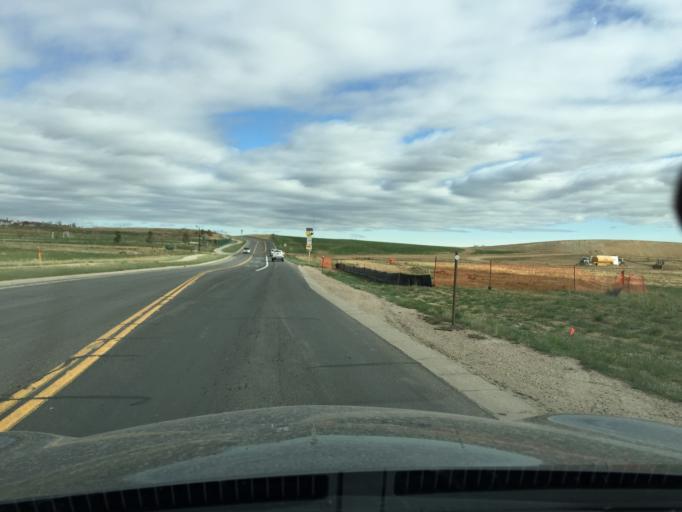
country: US
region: Colorado
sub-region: Boulder County
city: Erie
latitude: 40.0014
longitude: -105.0080
